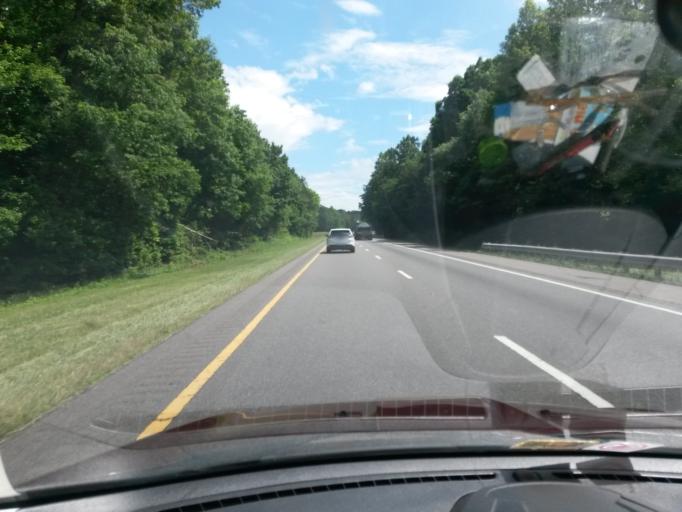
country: US
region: North Carolina
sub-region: Surry County
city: Dobson
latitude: 36.4311
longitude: -80.7769
